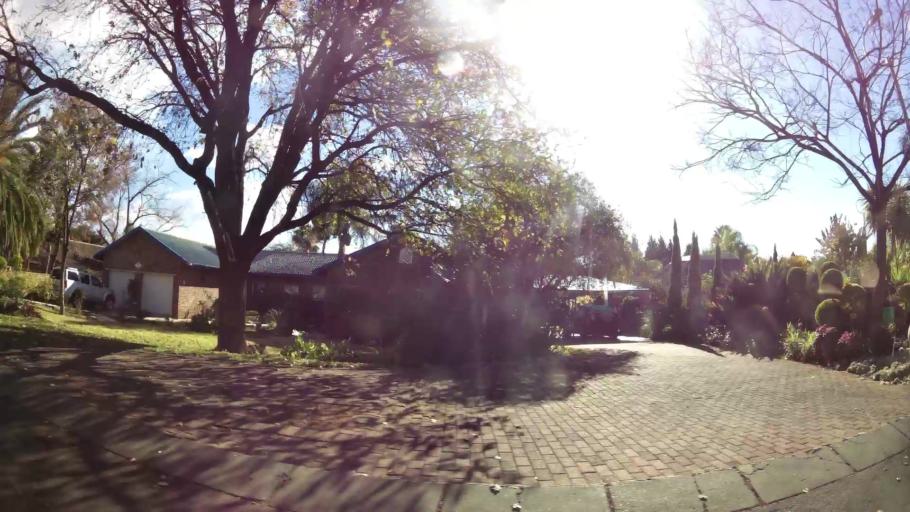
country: ZA
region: North-West
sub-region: Dr Kenneth Kaunda District Municipality
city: Klerksdorp
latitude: -26.8264
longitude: 26.6760
